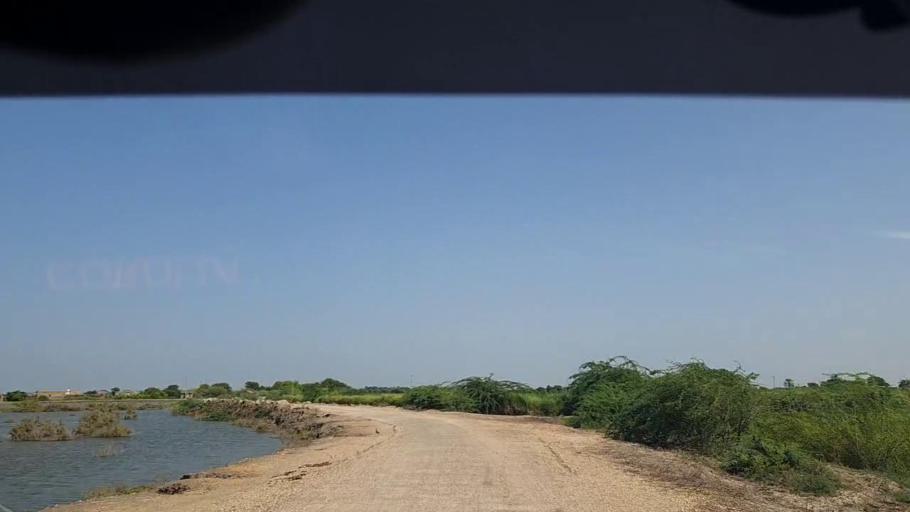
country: PK
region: Sindh
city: Badin
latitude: 24.4581
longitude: 68.7630
